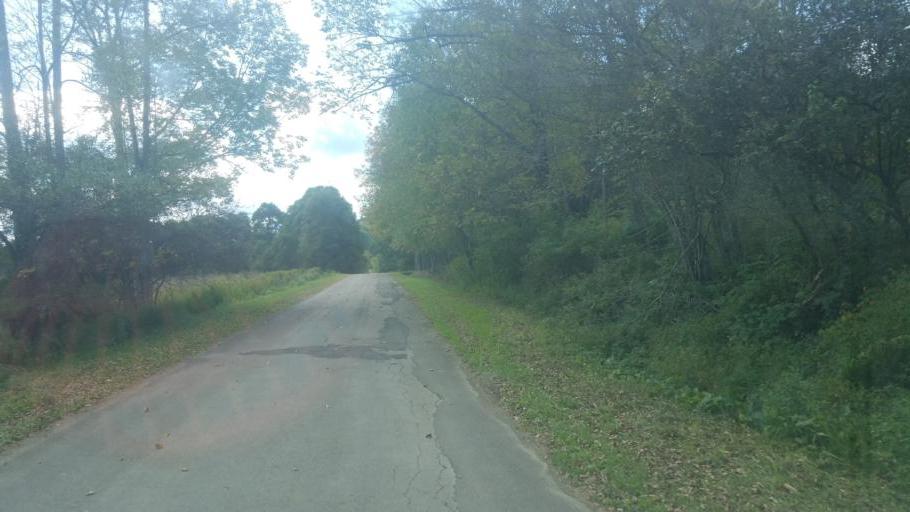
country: US
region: New York
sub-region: Cattaraugus County
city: Franklinville
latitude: 42.2145
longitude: -78.4146
